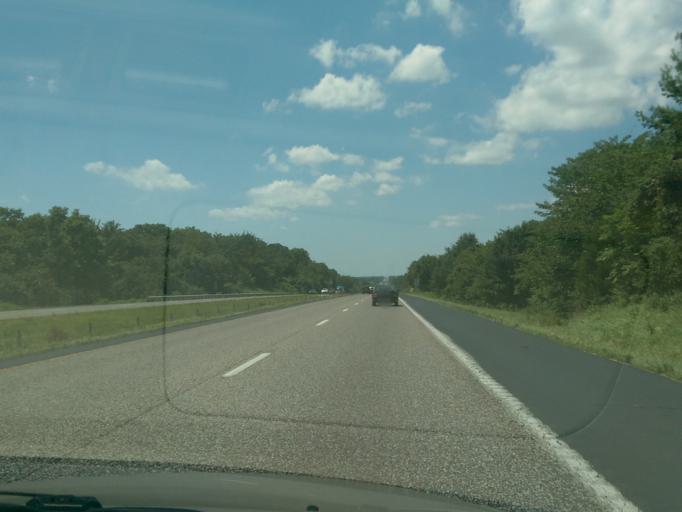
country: US
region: Missouri
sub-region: Cooper County
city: Boonville
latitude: 38.9396
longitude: -92.6052
